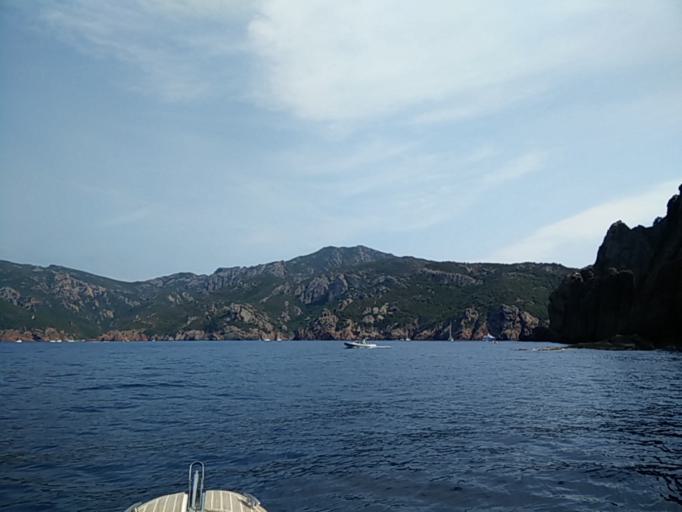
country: FR
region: Corsica
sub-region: Departement de la Corse-du-Sud
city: Cargese
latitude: 42.3801
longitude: 8.5509
